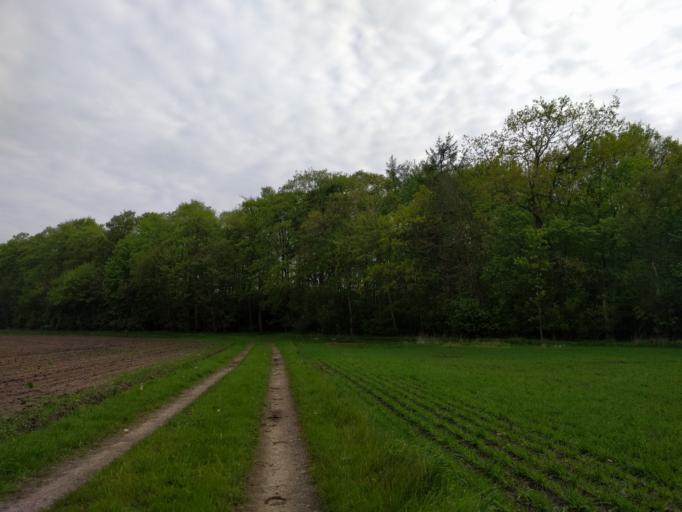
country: DK
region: South Denmark
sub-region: Kerteminde Kommune
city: Munkebo
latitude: 55.4203
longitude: 10.5415
